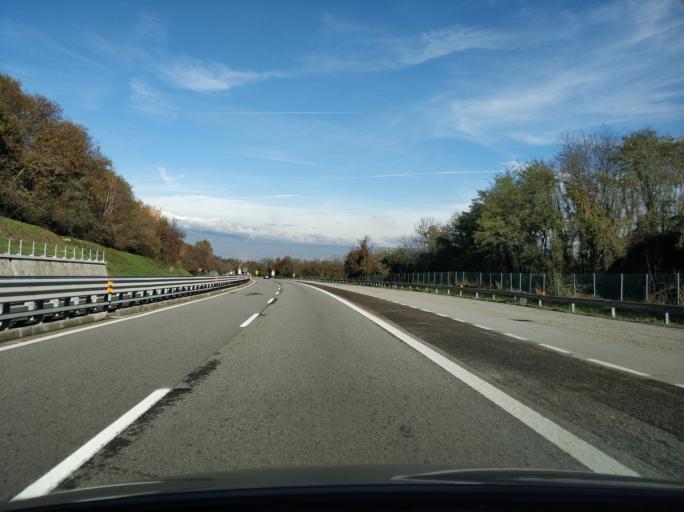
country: IT
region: Piedmont
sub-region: Provincia di Torino
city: Cuceglio
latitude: 45.3589
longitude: 7.8346
